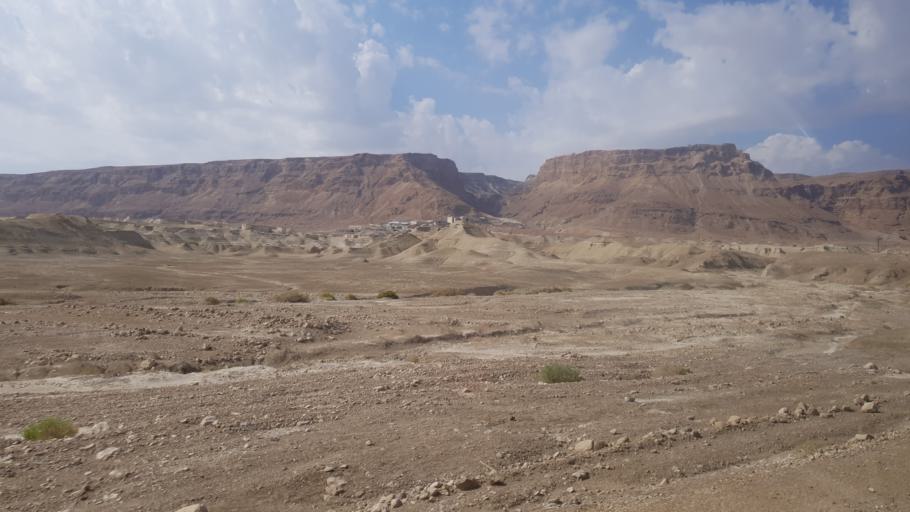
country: IL
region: Southern District
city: `En Boqeq
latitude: 31.3162
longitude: 35.3802
